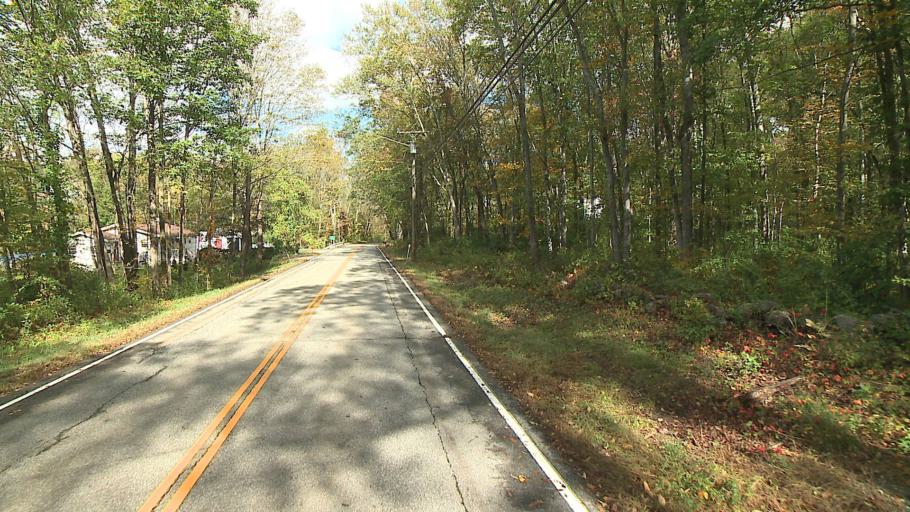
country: US
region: Connecticut
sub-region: Windham County
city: Putnam
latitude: 41.8852
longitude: -71.8755
